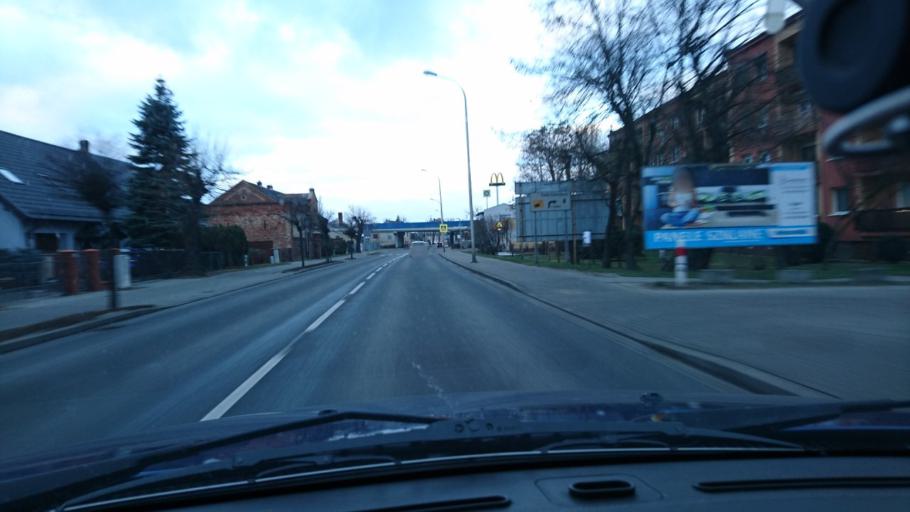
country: PL
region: Greater Poland Voivodeship
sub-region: Powiat kepinski
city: Kepno
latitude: 51.2869
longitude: 17.9931
